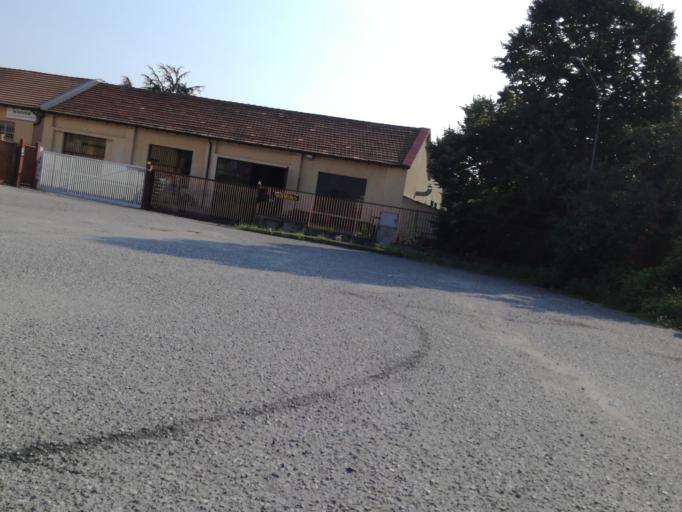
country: IT
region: Lombardy
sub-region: Provincia di Lecco
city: Paderno d'Adda
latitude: 45.6783
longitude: 9.4370
